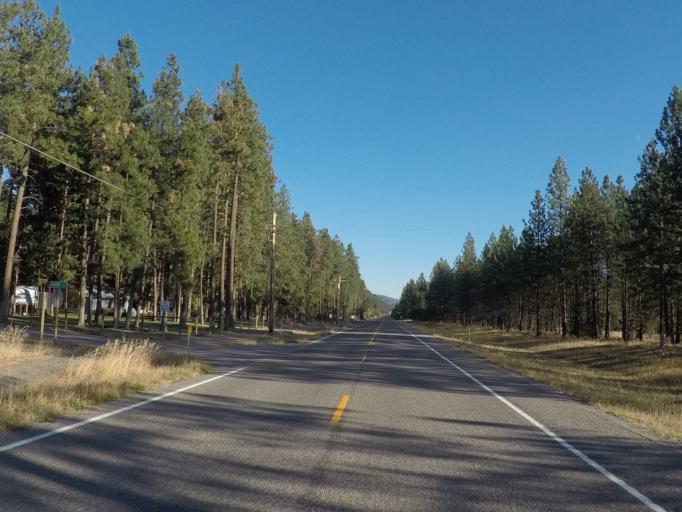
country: US
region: Montana
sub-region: Missoula County
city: Bonner-West Riverside
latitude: 46.8440
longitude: -113.8408
